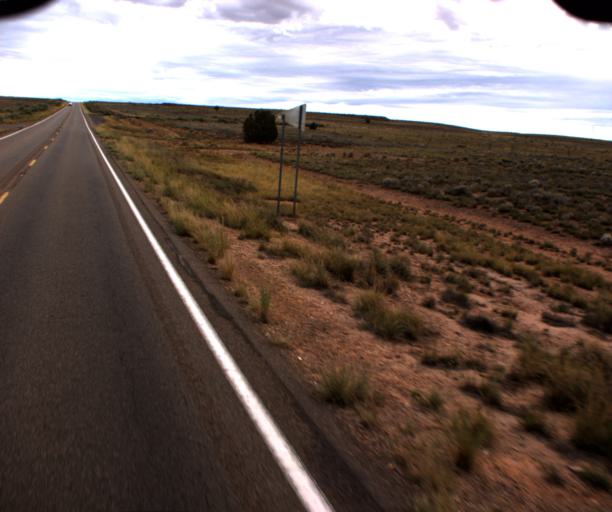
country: US
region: Arizona
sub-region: Navajo County
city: Holbrook
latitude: 34.8334
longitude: -110.1442
